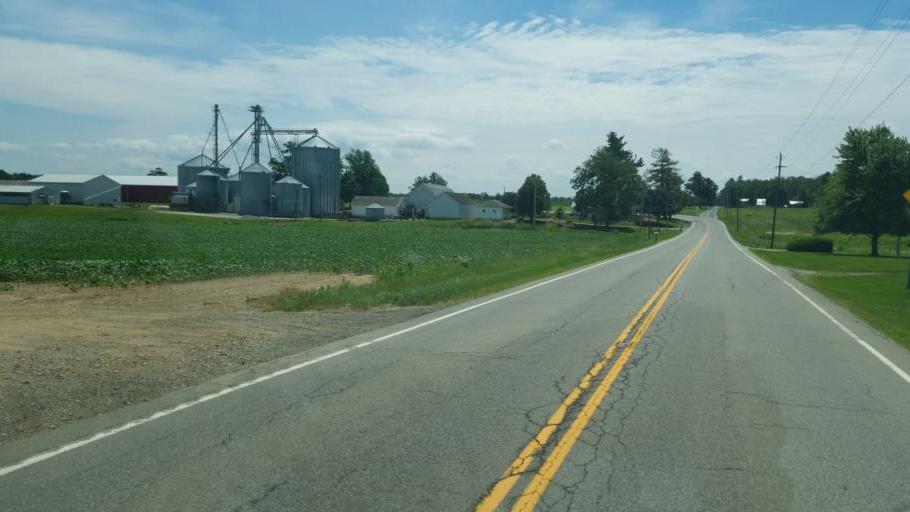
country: US
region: Ohio
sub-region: Richland County
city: Lincoln Heights
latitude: 40.8898
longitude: -82.5326
